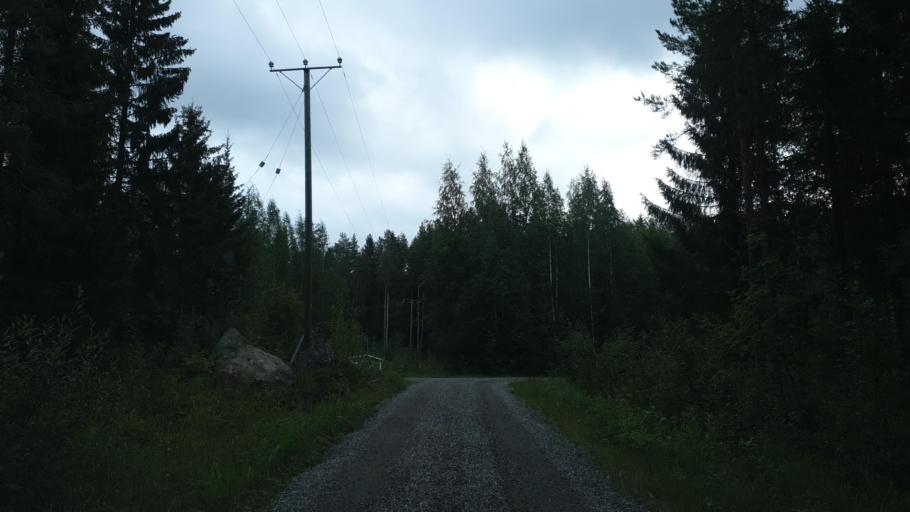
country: FI
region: Northern Savo
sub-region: Kuopio
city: Nilsiae
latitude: 63.2492
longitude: 28.2546
